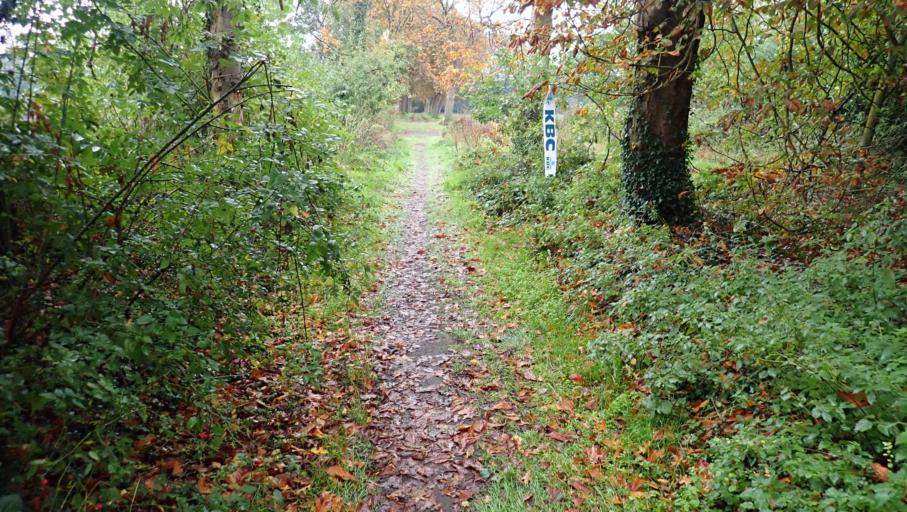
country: BE
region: Flanders
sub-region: Provincie Antwerpen
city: Nijlen
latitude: 51.1438
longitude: 4.6734
